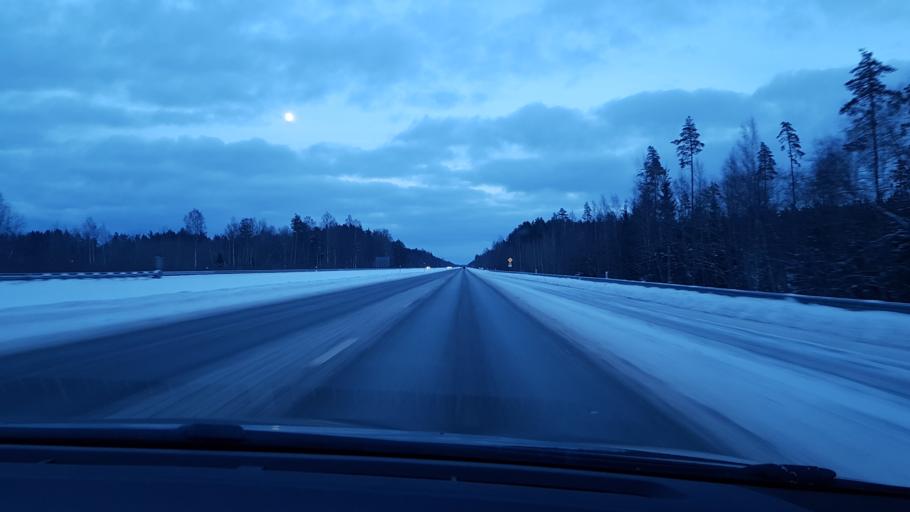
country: EE
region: Harju
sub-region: Kuusalu vald
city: Kuusalu
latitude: 59.4567
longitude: 25.5287
